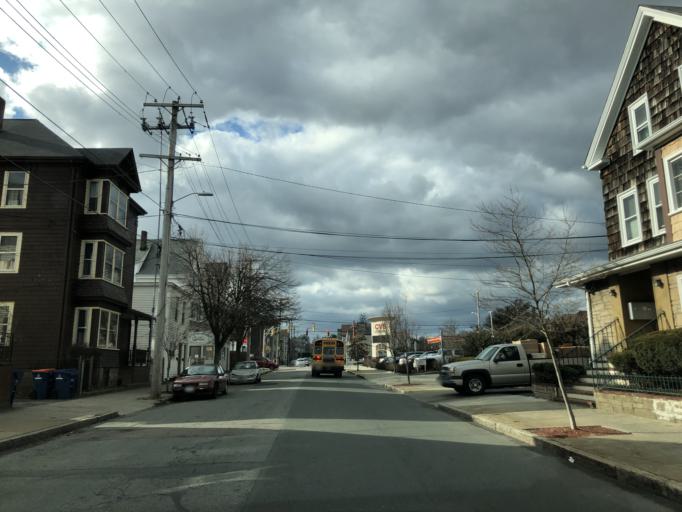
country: US
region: Massachusetts
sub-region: Bristol County
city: New Bedford
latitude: 41.6575
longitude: -70.9281
